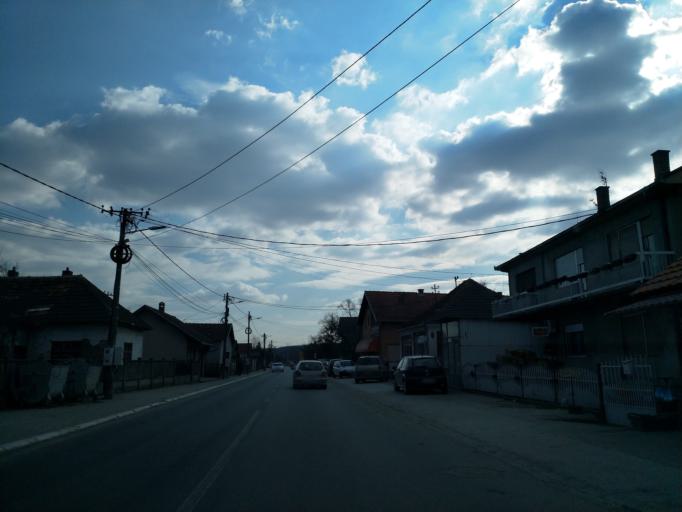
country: RS
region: Central Serbia
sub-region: Sumadijski Okrug
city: Batocina
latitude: 44.1503
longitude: 21.0776
